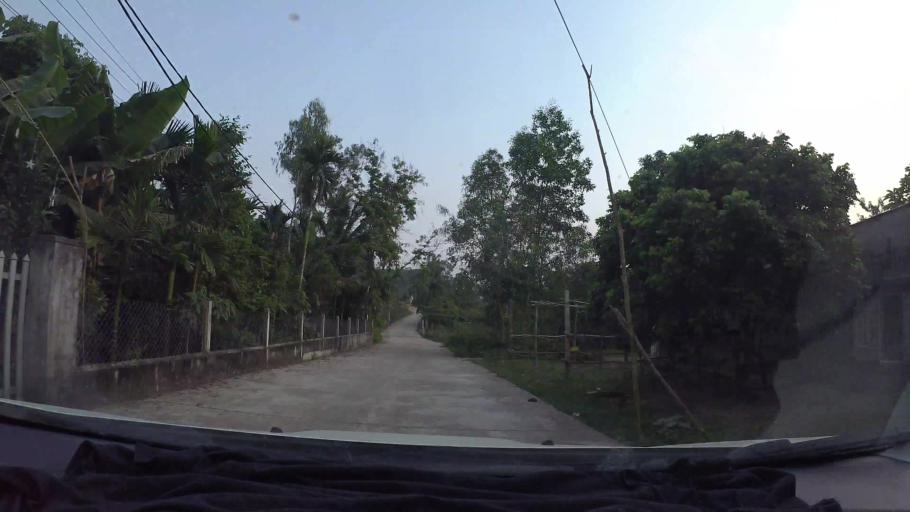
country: VN
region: Da Nang
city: Lien Chieu
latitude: 16.0550
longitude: 108.1072
